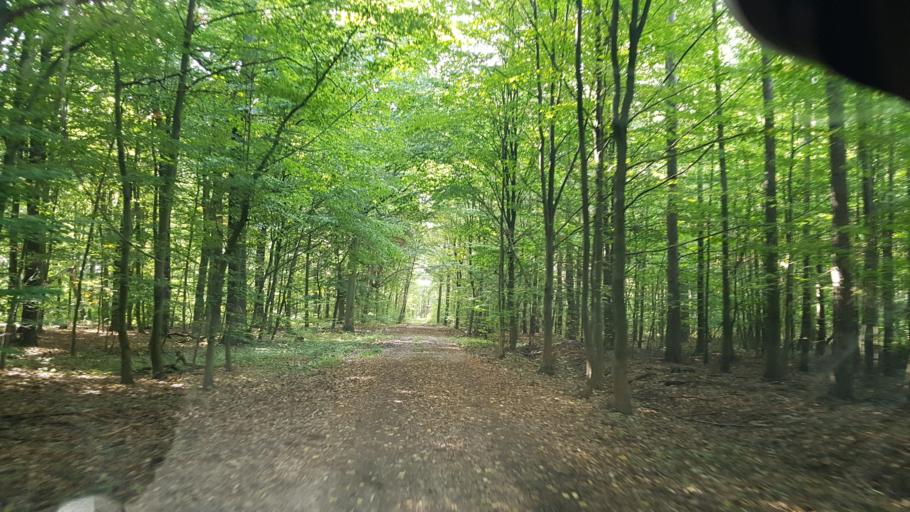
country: DE
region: Brandenburg
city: Doberlug-Kirchhain
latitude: 51.6178
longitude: 13.5411
